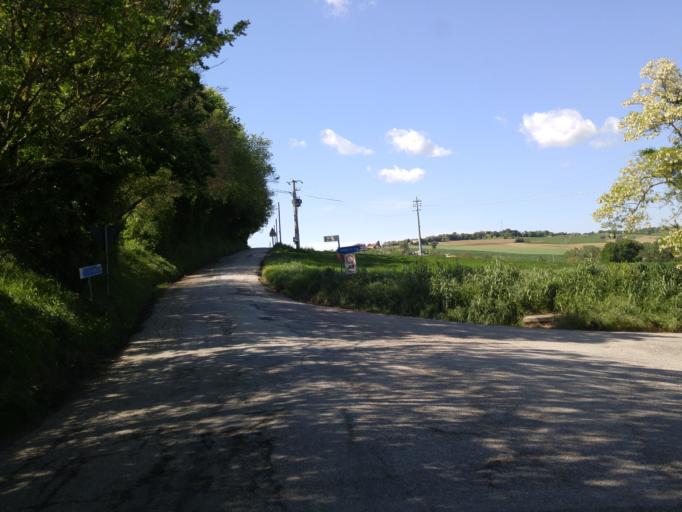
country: IT
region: The Marches
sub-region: Provincia di Pesaro e Urbino
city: Cartoceto
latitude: 43.7813
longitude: 12.9031
